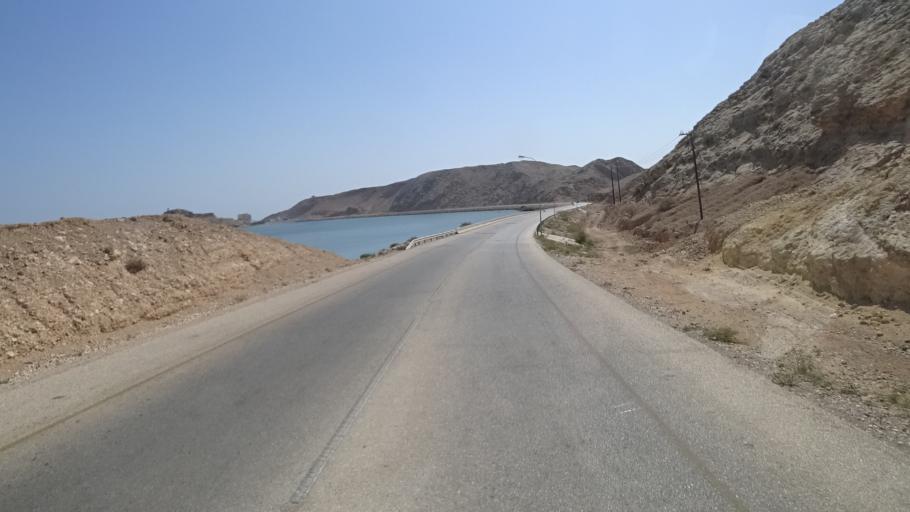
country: OM
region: Ash Sharqiyah
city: Sur
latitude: 22.5526
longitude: 59.5319
